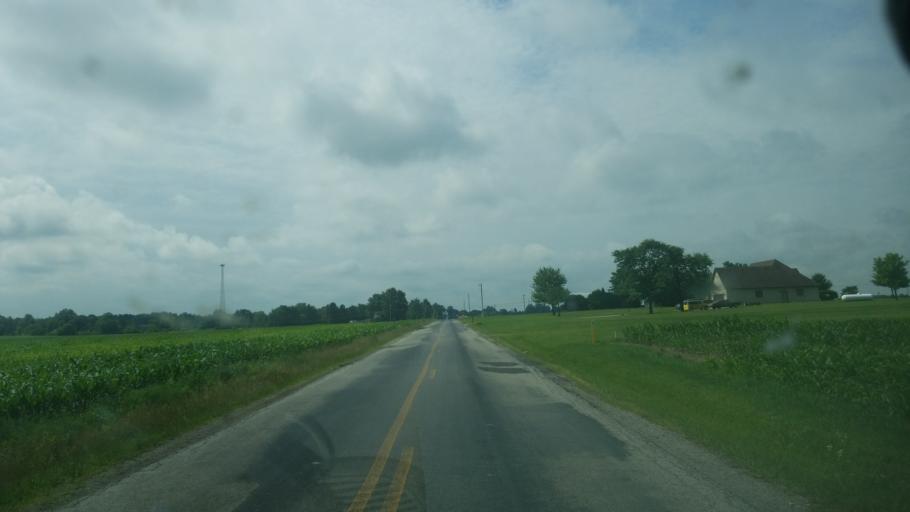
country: US
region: Ohio
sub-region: Licking County
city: Johnstown
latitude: 40.1928
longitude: -82.7570
